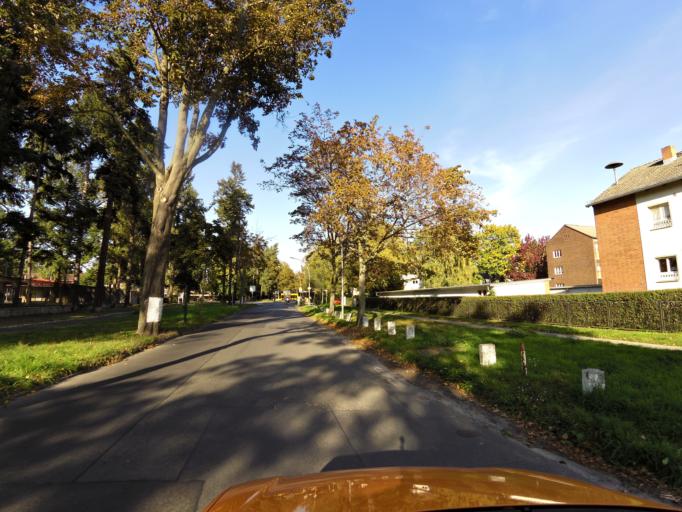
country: DE
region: Berlin
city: Kladow
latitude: 52.4465
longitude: 13.1266
